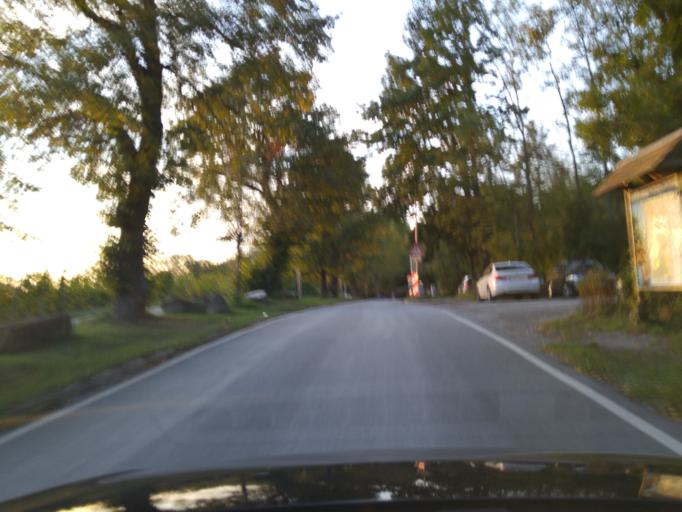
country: DE
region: Baden-Wuerttemberg
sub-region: Regierungsbezirk Stuttgart
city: Heilbronn
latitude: 49.1582
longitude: 9.2374
